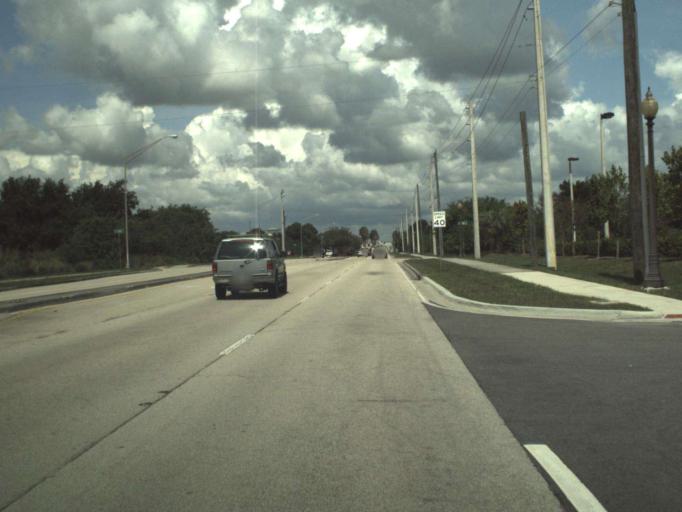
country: US
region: Florida
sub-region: Saint Lucie County
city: River Park
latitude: 27.3179
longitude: -80.3657
